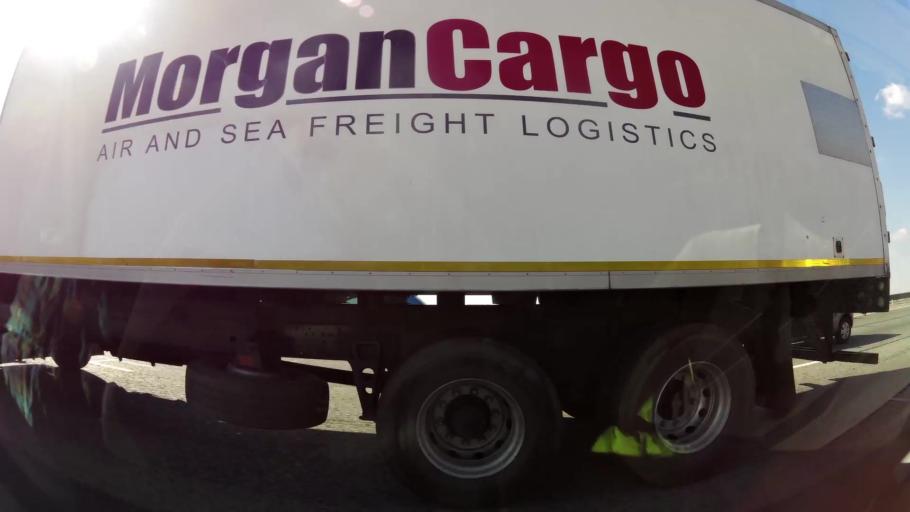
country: ZA
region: Gauteng
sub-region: Ekurhuleni Metropolitan Municipality
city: Tembisa
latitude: -26.0537
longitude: 28.2811
